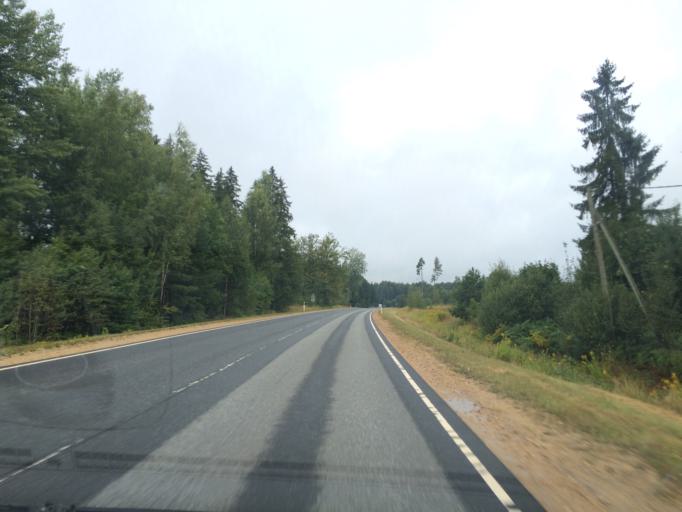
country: LV
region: Ogre
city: Ogre
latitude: 56.8564
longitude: 24.5964
